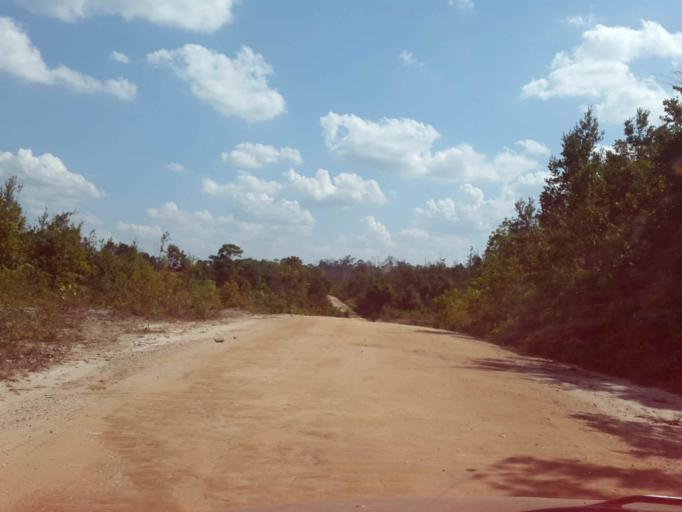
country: MY
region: Sarawak
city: Simanggang
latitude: 0.7375
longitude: 111.5713
